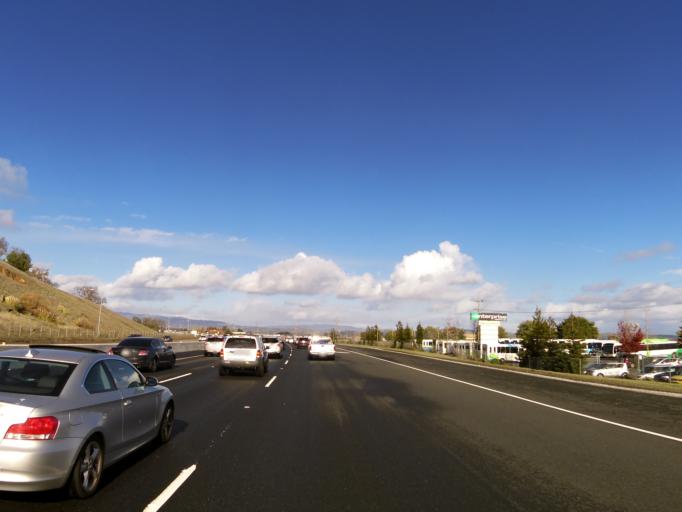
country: US
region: California
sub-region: Marin County
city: Novato
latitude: 38.1287
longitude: -122.5646
